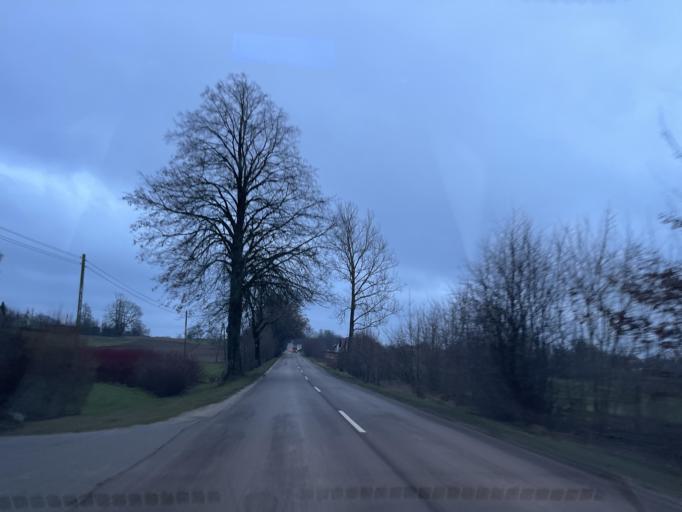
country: PL
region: Pomeranian Voivodeship
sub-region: Powiat kartuski
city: Kartuzy
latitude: 54.4072
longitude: 18.2133
